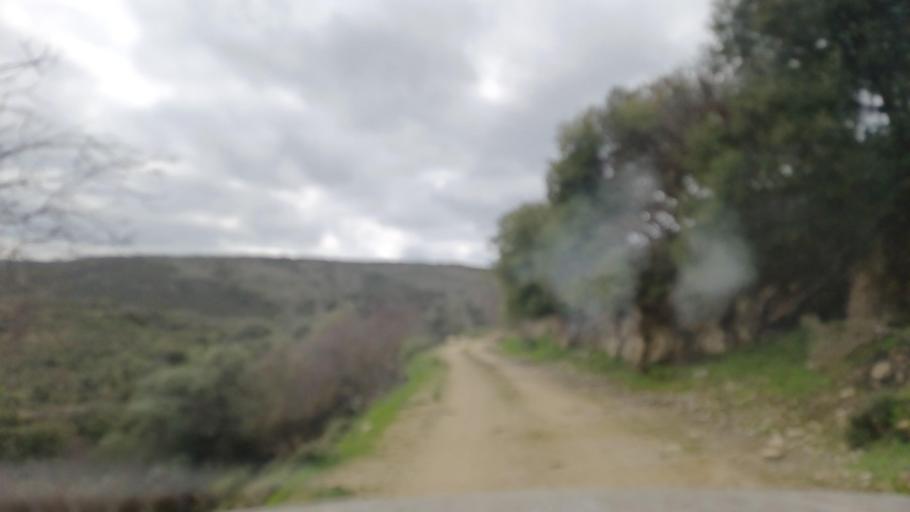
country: CY
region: Limassol
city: Pissouri
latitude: 34.7658
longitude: 32.6811
